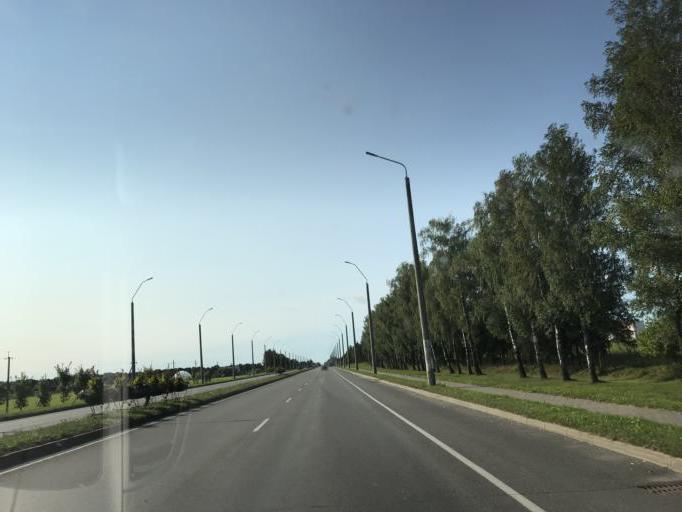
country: BY
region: Mogilev
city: Buynichy
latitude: 53.8692
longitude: 30.2615
